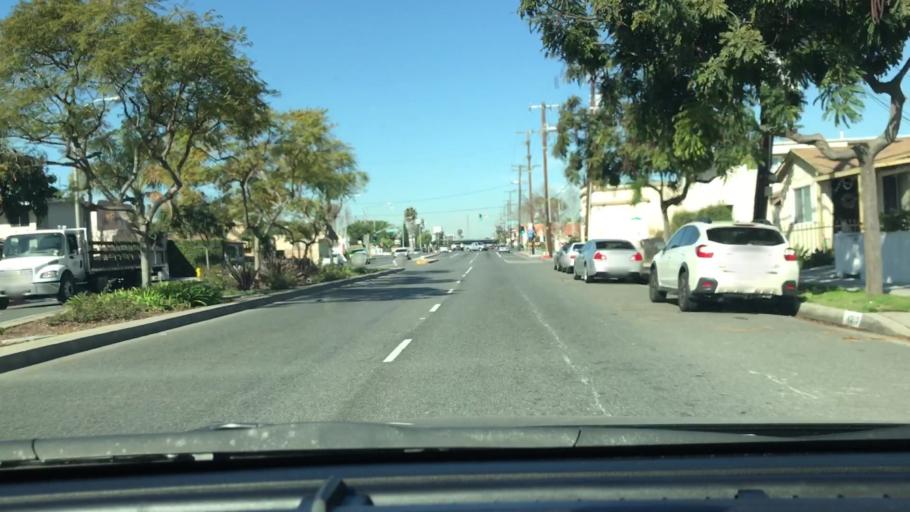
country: US
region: California
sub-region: Los Angeles County
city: Lawndale
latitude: 33.8875
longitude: -118.3507
